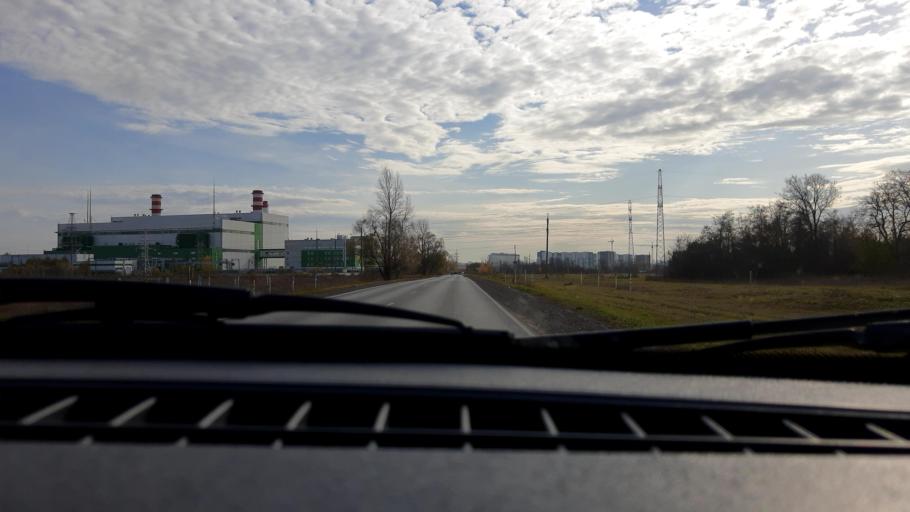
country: RU
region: Bashkortostan
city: Mikhaylovka
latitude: 54.8030
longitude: 55.8290
